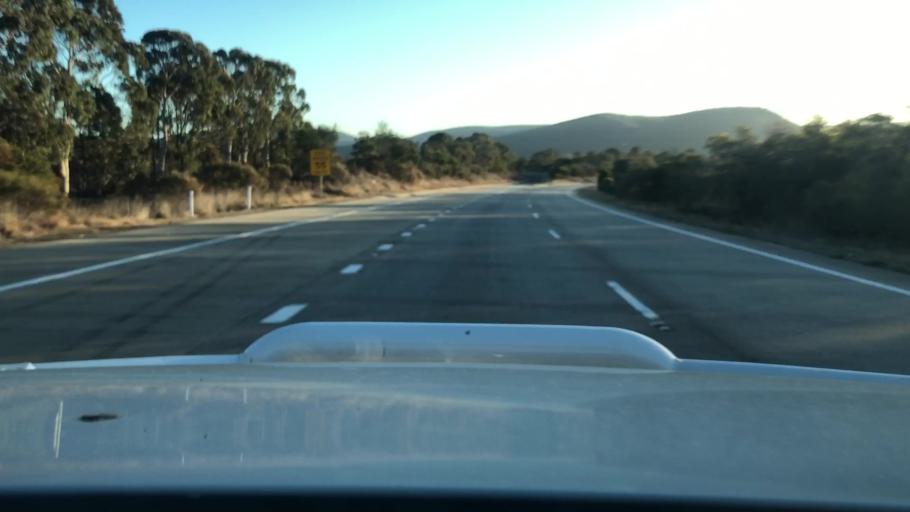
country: AU
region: New South Wales
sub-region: Goulburn Mulwaree
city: Goulburn
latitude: -34.7462
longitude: 149.7695
